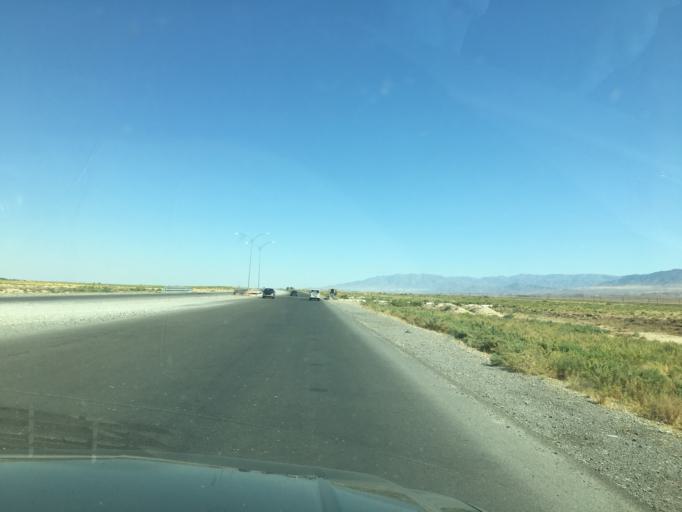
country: TM
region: Balkan
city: Serdar
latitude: 38.7690
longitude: 56.7382
